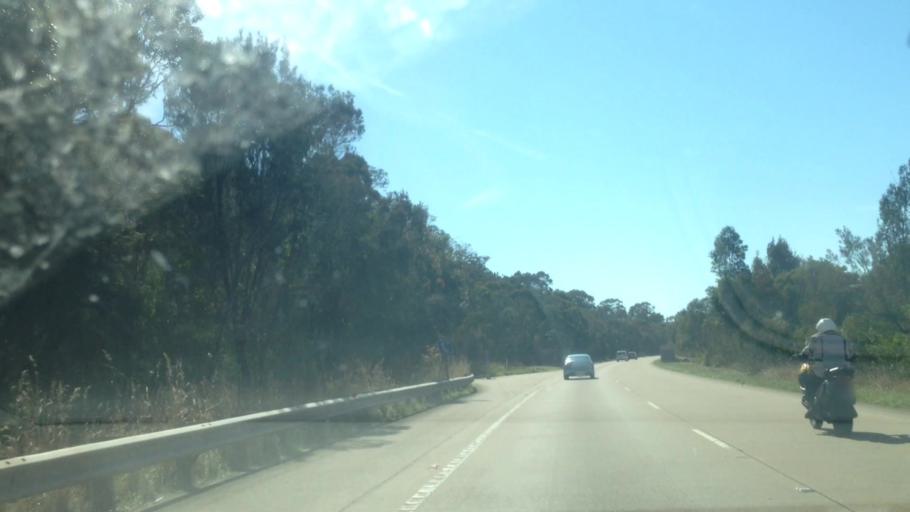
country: AU
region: New South Wales
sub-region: Lake Macquarie Shire
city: Holmesville
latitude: -32.8966
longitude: 151.5722
